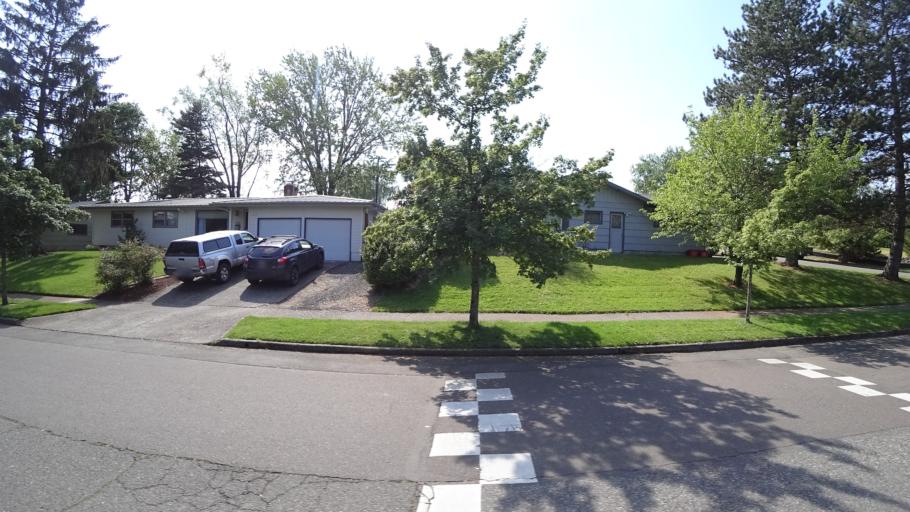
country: US
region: Oregon
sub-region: Washington County
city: Beaverton
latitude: 45.4682
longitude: -122.7915
